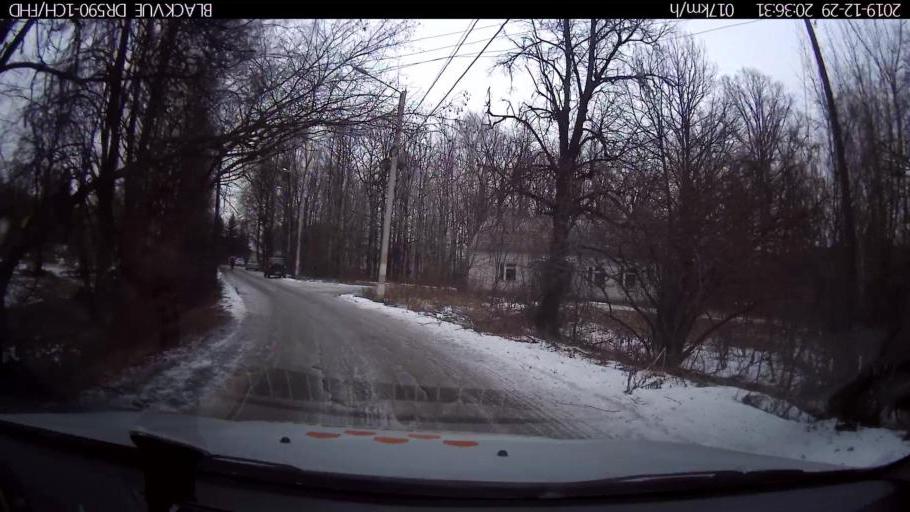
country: RU
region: Nizjnij Novgorod
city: Afonino
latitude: 56.1924
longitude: 44.0483
